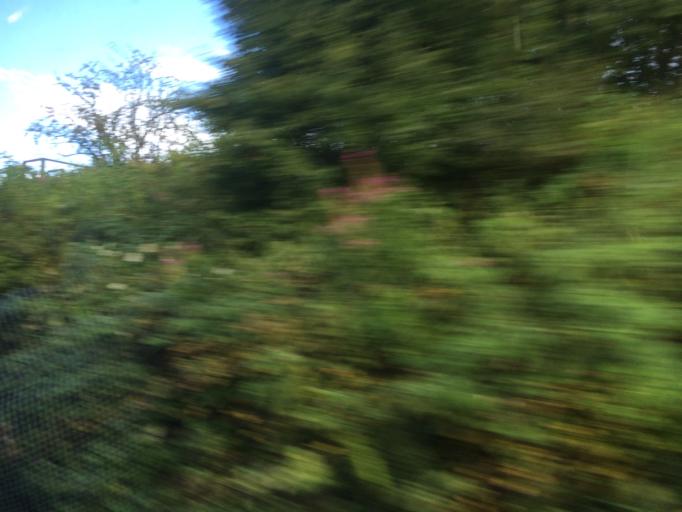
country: GB
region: Scotland
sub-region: Falkirk
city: Larbert
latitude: 56.0027
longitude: -3.8407
